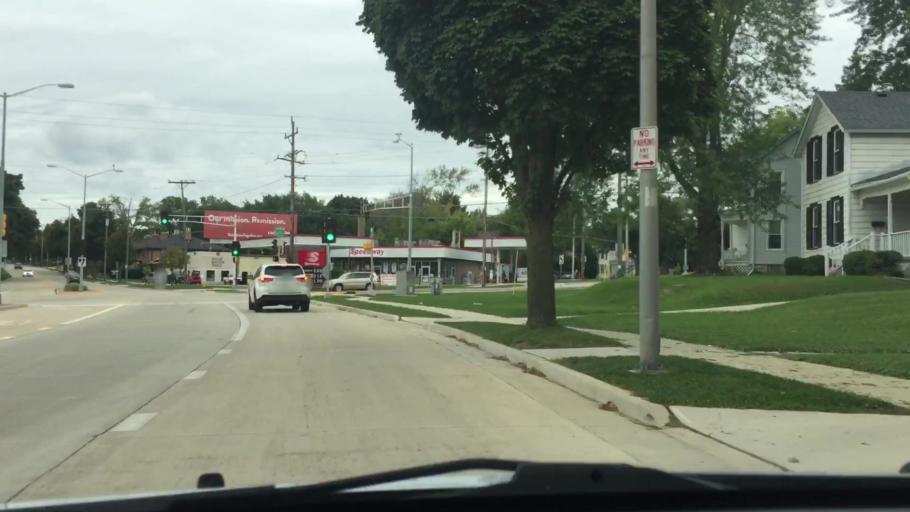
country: US
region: Wisconsin
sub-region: Waukesha County
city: Waukesha
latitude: 43.0181
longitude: -88.2383
